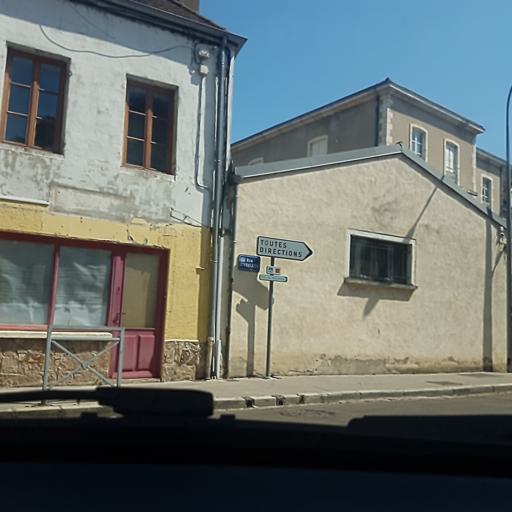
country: FR
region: Bourgogne
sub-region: Departement de Saone-et-Loire
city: Chalon-sur-Saone
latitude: 46.7788
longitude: 4.8605
